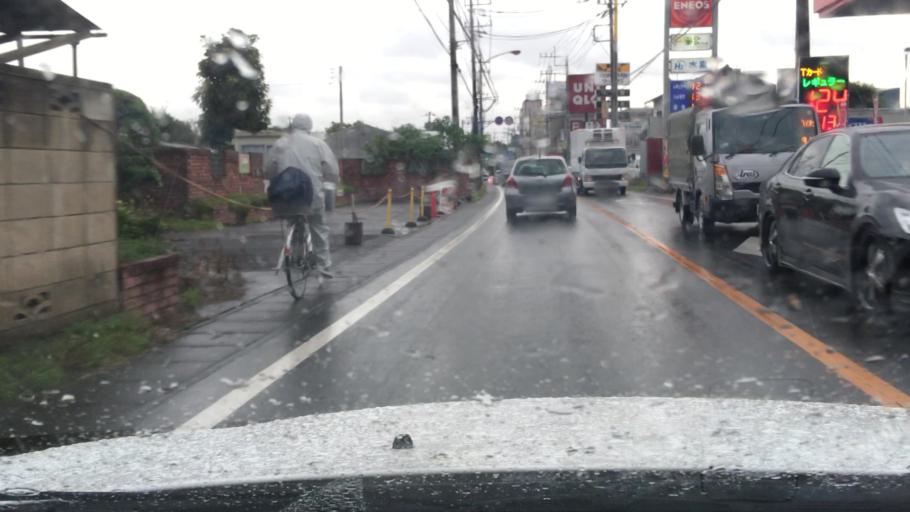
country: JP
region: Saitama
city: Saitama
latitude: 35.9217
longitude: 139.6528
